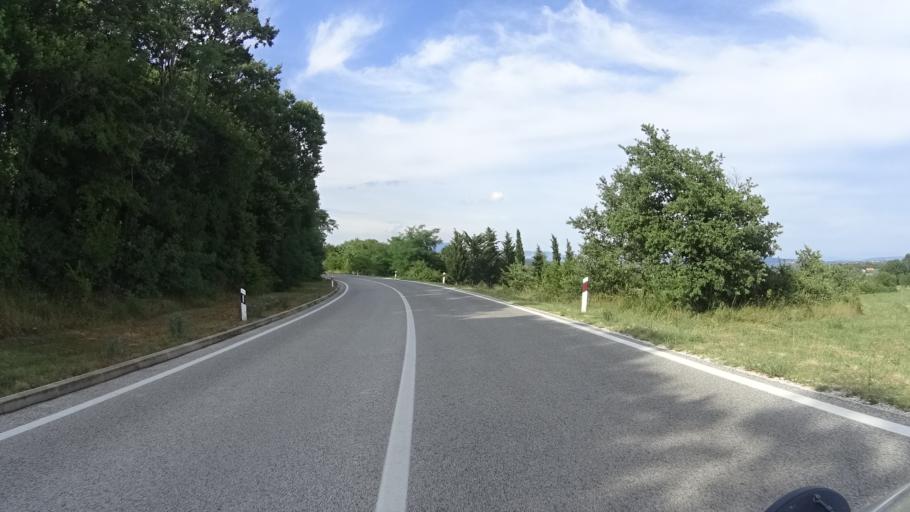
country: HR
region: Istarska
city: Rasa
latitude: 45.0521
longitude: 14.0133
